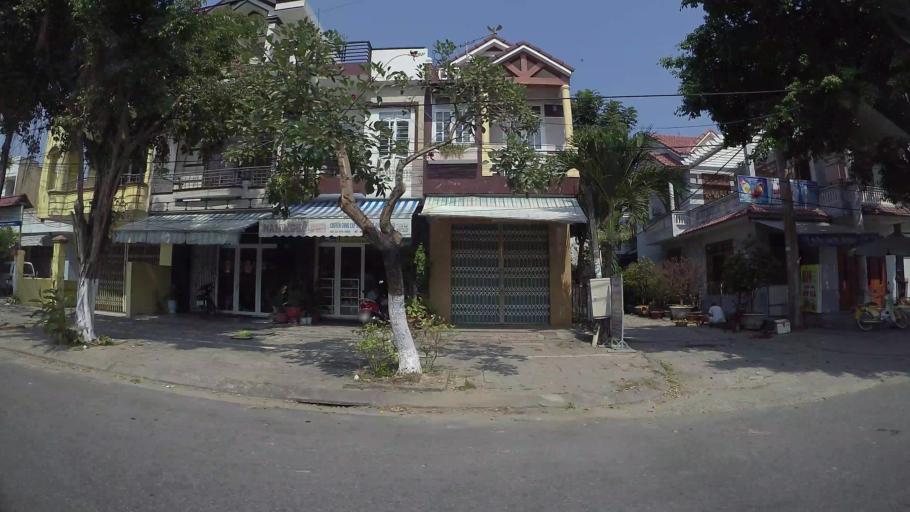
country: VN
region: Da Nang
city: Ngu Hanh Son
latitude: 16.0111
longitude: 108.2569
